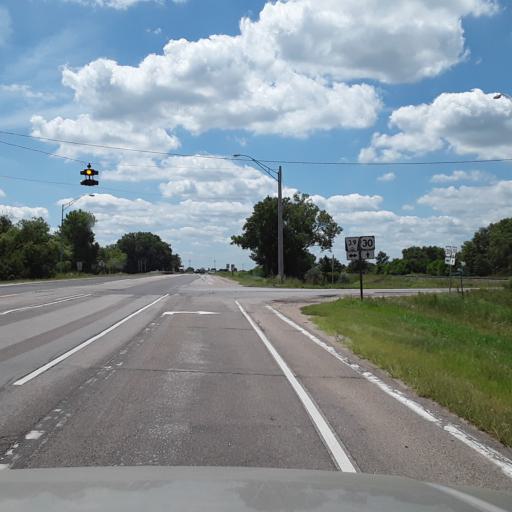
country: US
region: Nebraska
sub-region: Nance County
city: Genoa
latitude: 41.3125
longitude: -97.6709
